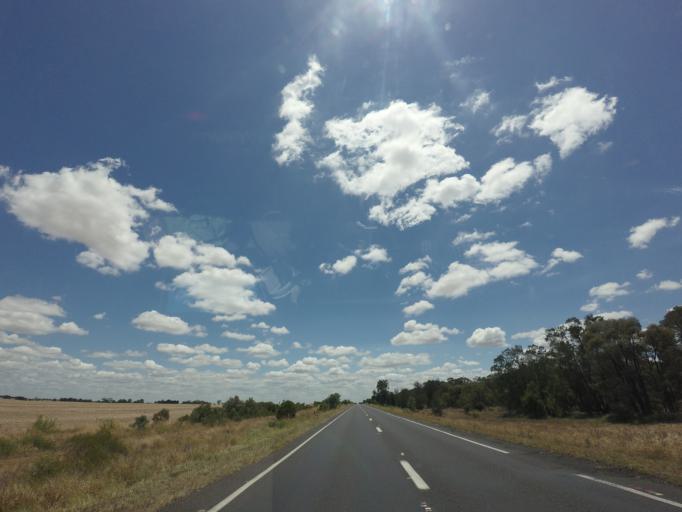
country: AU
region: New South Wales
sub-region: Moree Plains
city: Boggabilla
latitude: -28.8159
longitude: 150.2372
